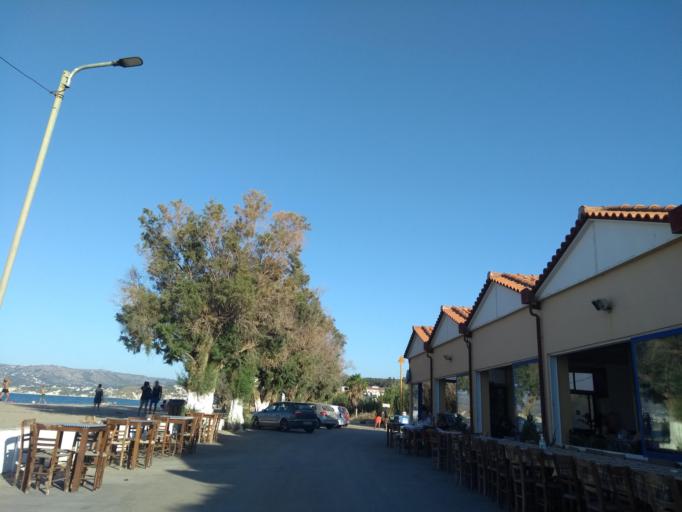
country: GR
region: Crete
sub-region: Nomos Chanias
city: Kalivai
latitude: 35.4637
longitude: 24.1580
